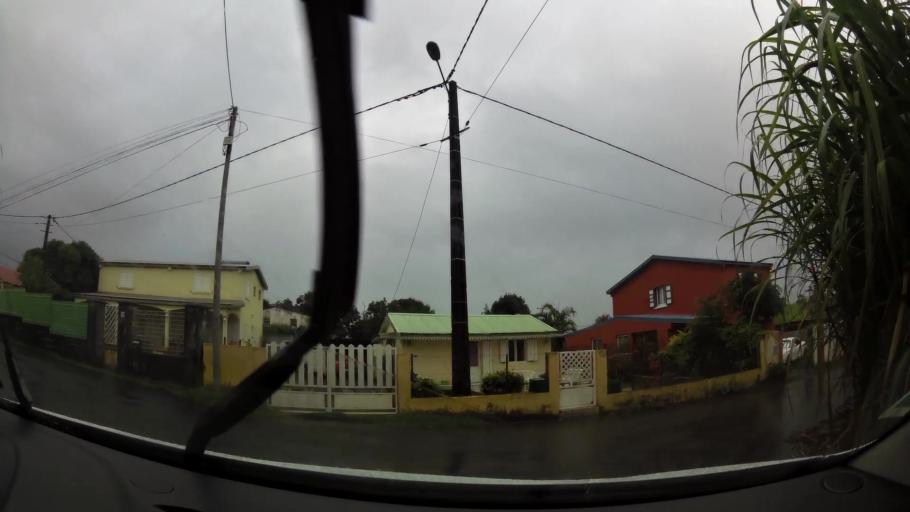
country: RE
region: Reunion
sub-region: Reunion
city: Saint-Benoit
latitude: -21.0218
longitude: 55.6962
